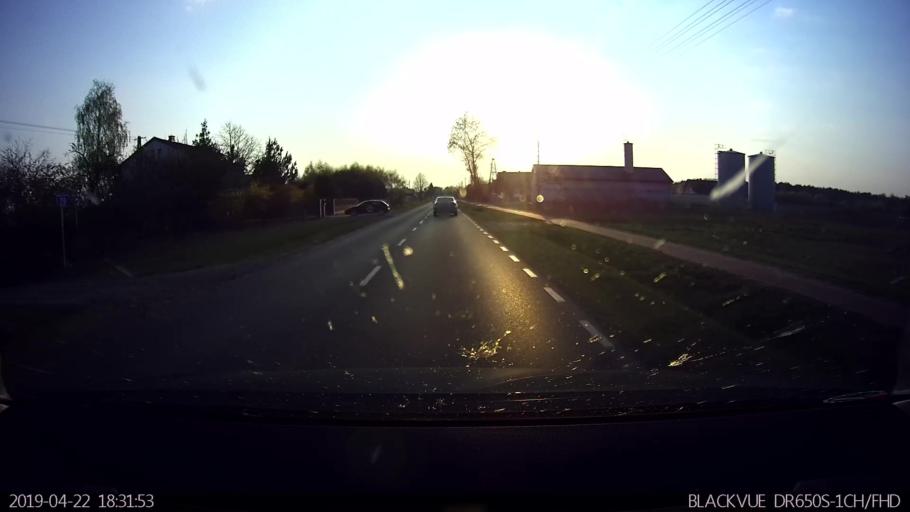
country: PL
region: Masovian Voivodeship
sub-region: Powiat wolominski
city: Tluszcz
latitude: 52.4515
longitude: 21.4105
